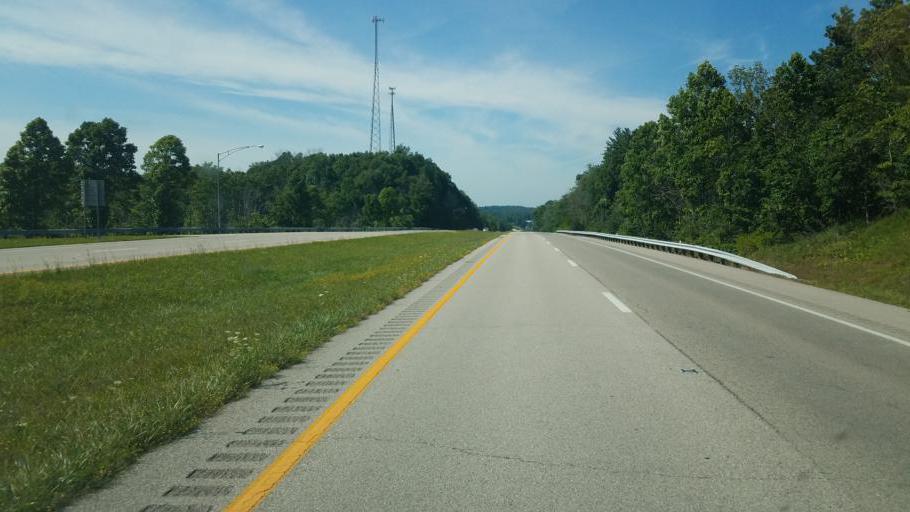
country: US
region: Ohio
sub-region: Meigs County
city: Pomeroy
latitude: 39.1277
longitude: -82.0190
